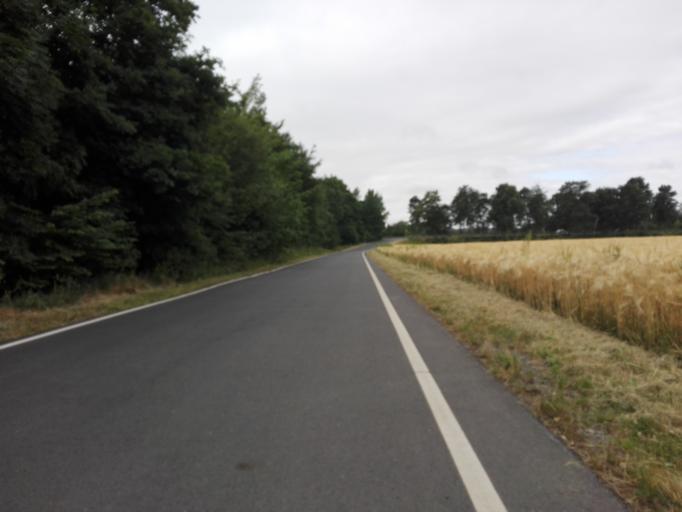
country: DE
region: North Rhine-Westphalia
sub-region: Regierungsbezirk Arnsberg
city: Unna
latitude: 51.5220
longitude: 7.6994
